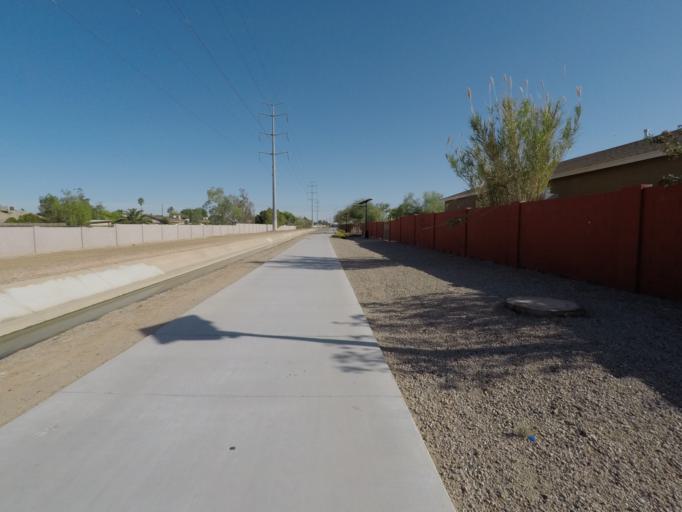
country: US
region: Arizona
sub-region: Maricopa County
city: Guadalupe
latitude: 33.3659
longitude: -111.9569
